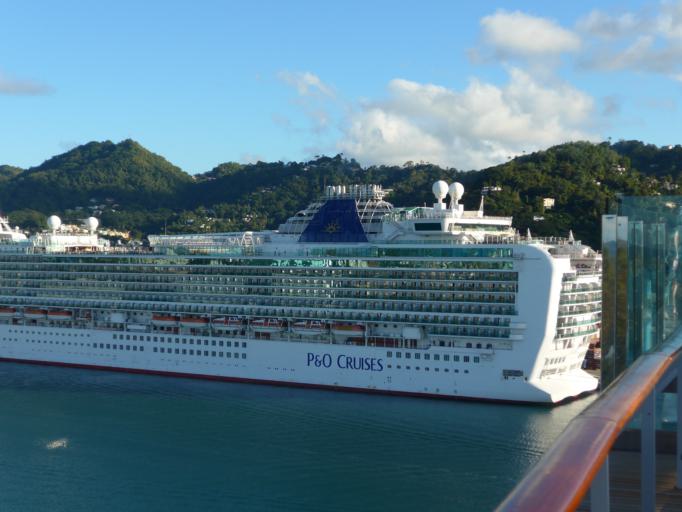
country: LC
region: Castries Quarter
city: Castries
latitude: 14.0141
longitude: -60.9947
